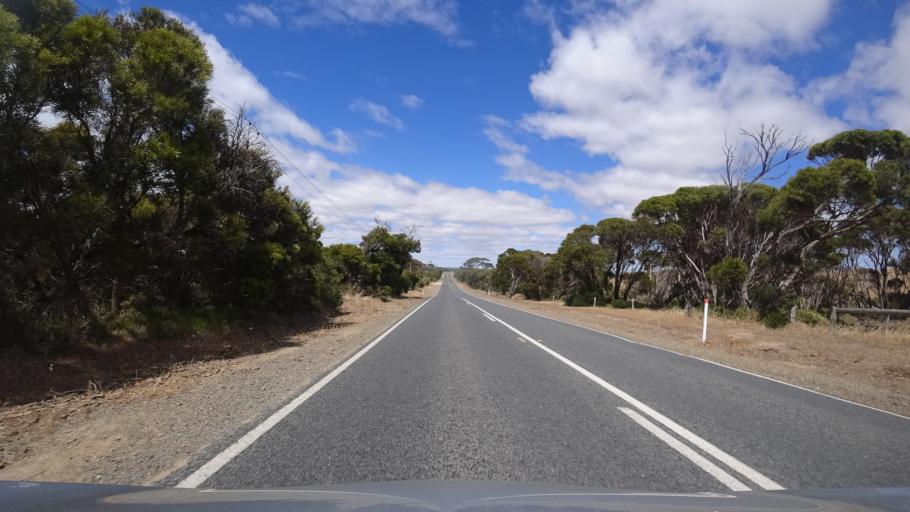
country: AU
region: South Australia
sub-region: Kangaroo Island
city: Kingscote
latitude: -35.6640
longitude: 137.5985
